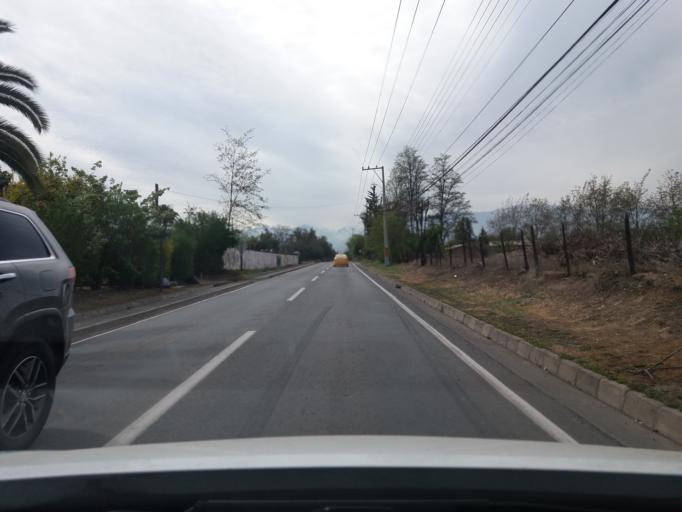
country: CL
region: Valparaiso
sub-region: Provincia de Los Andes
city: Los Andes
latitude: -32.8234
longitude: -70.6659
